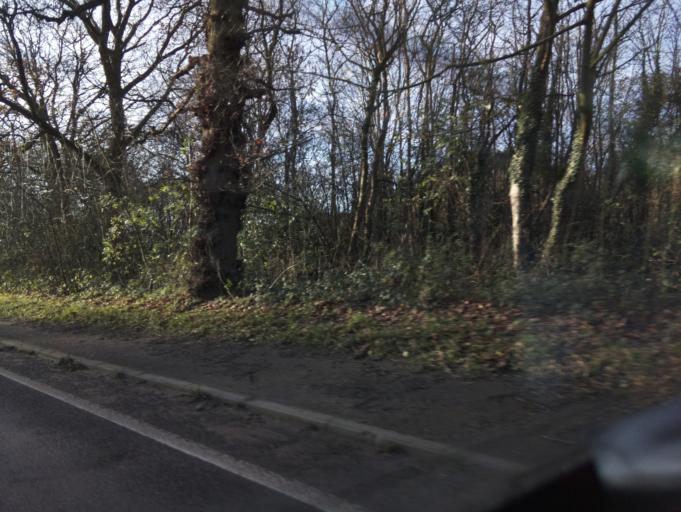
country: GB
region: England
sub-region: City and Borough of Birmingham
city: Sutton Coldfield
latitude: 52.5878
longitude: -1.7803
